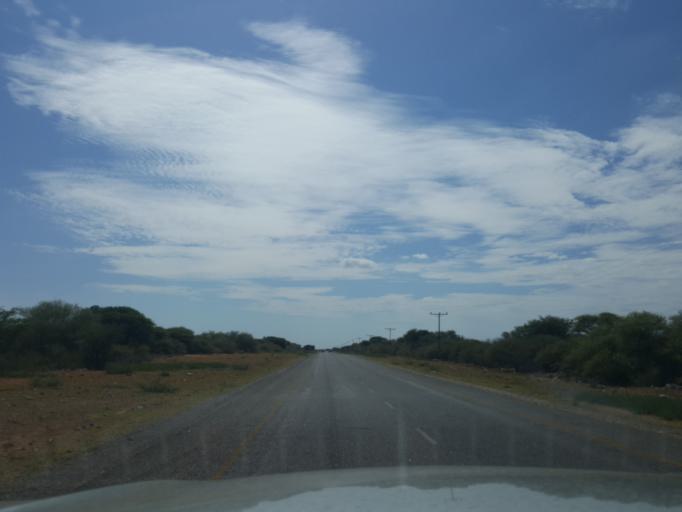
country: BW
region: Kweneng
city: Letlhakeng
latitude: -24.1432
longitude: 25.1475
